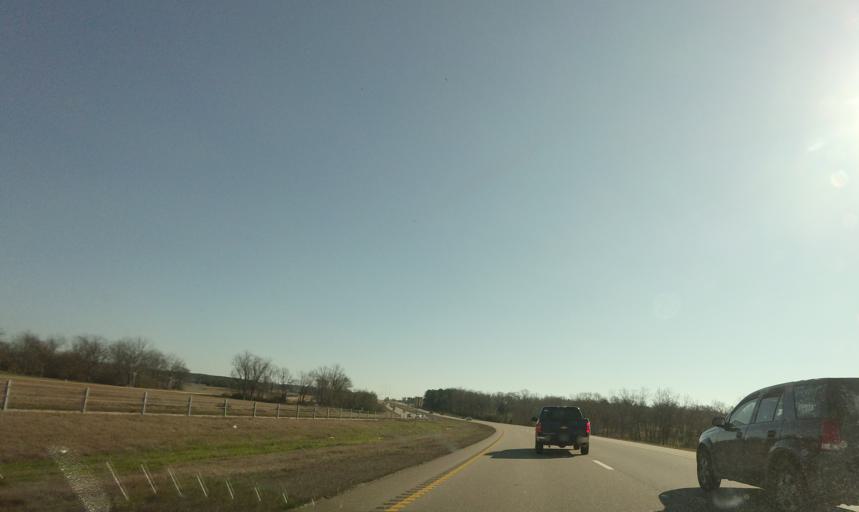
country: US
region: Mississippi
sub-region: Marshall County
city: Holly Springs
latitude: 34.7552
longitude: -89.4652
